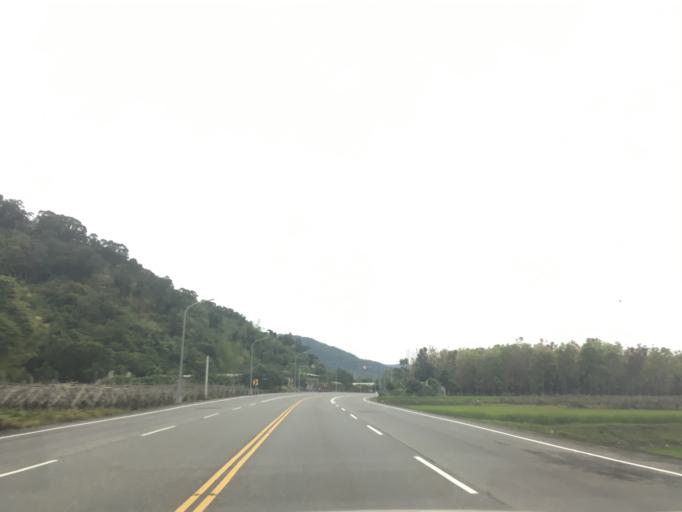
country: TW
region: Taiwan
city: Taitung City
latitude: 22.7383
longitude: 121.0566
